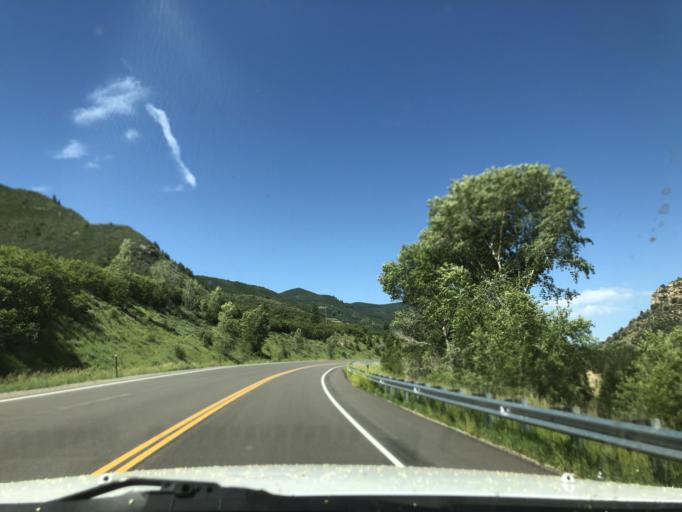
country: US
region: Colorado
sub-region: Delta County
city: Paonia
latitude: 38.9286
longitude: -107.4216
